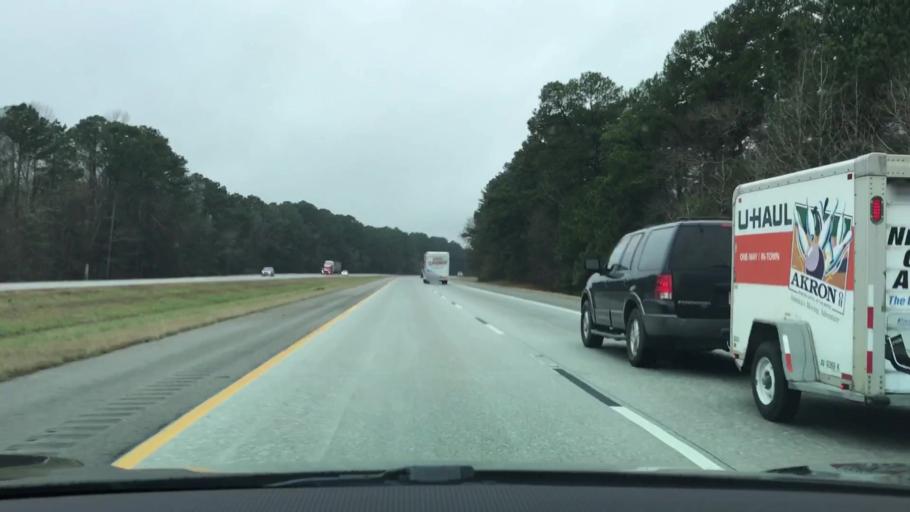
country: US
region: Georgia
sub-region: Putnam County
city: Jefferson
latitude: 33.5331
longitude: -83.2872
